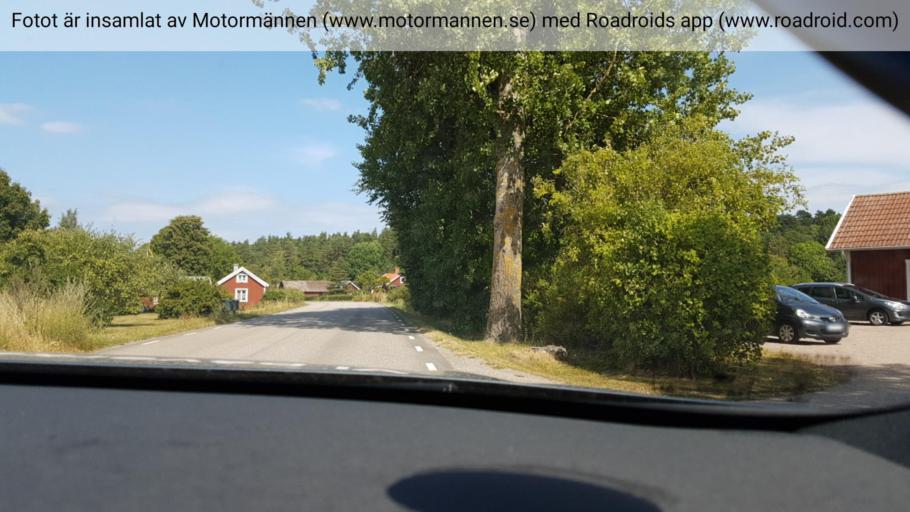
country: SE
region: Vaestra Goetaland
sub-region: Gotene Kommun
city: Kallby
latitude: 58.5204
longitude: 13.3217
